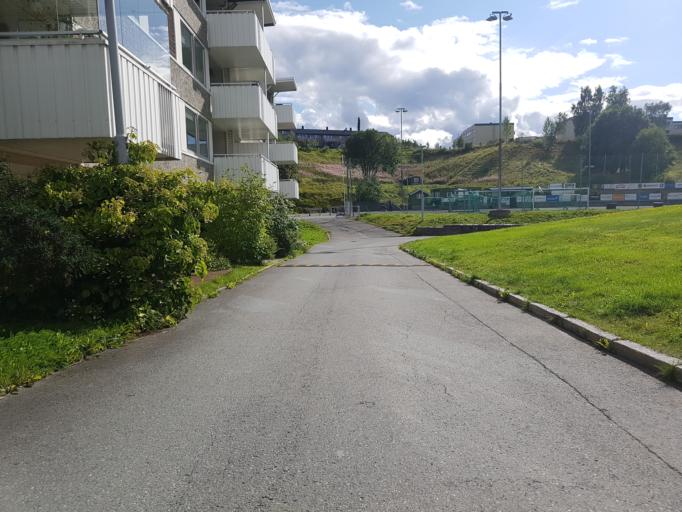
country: NO
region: Sor-Trondelag
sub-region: Trondheim
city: Trondheim
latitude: 63.4049
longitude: 10.4413
